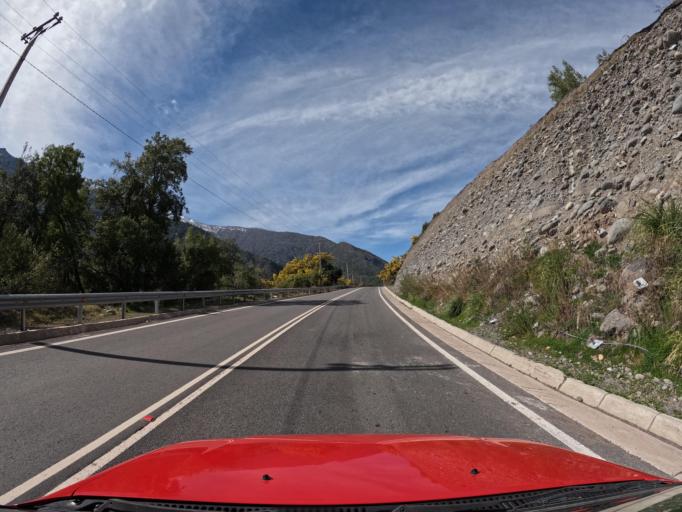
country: CL
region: O'Higgins
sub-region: Provincia de Colchagua
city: Chimbarongo
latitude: -34.9987
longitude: -70.8207
